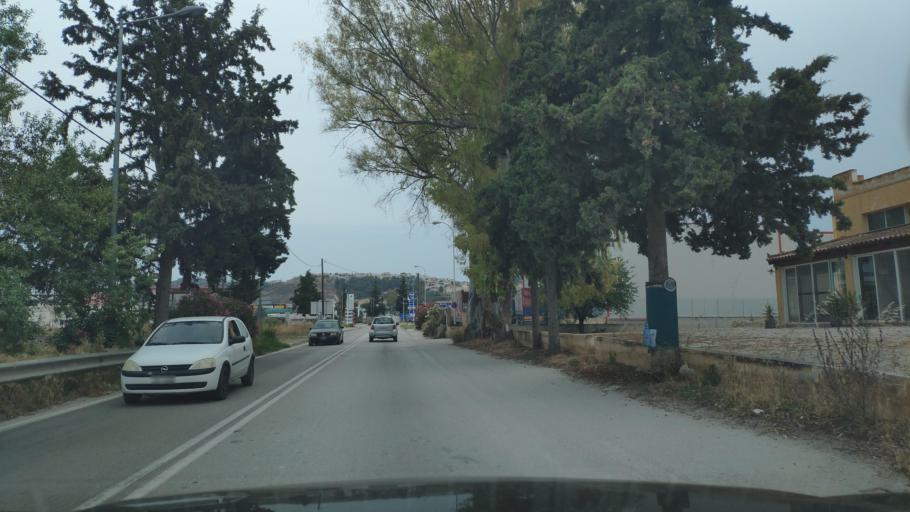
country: GR
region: Peloponnese
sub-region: Nomos Argolidos
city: Kranidi
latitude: 37.3948
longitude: 23.1569
